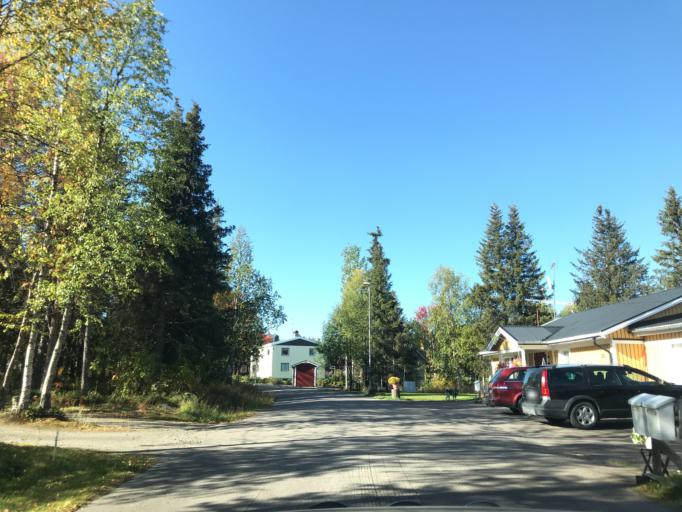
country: SE
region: Norrbotten
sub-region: Gallivare Kommun
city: Malmberget
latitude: 67.6471
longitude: 21.0696
